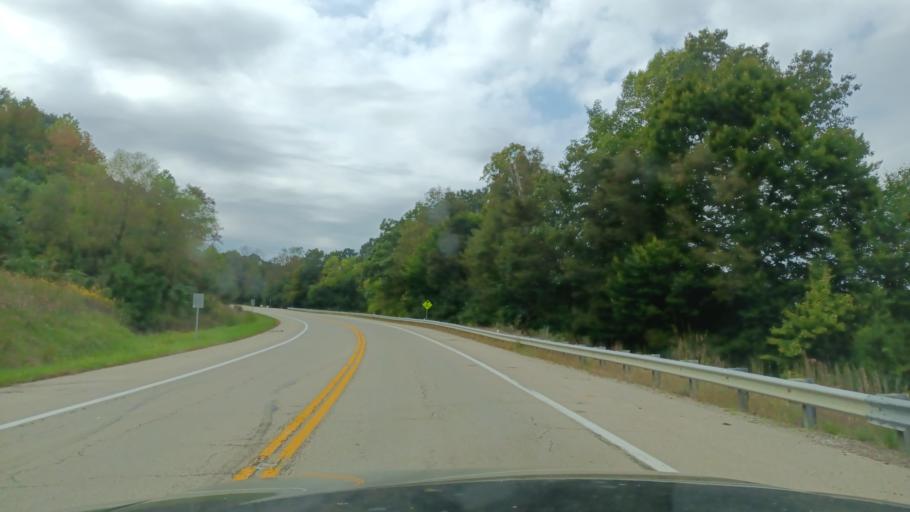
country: US
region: Ohio
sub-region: Vinton County
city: McArthur
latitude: 39.2799
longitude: -82.5340
